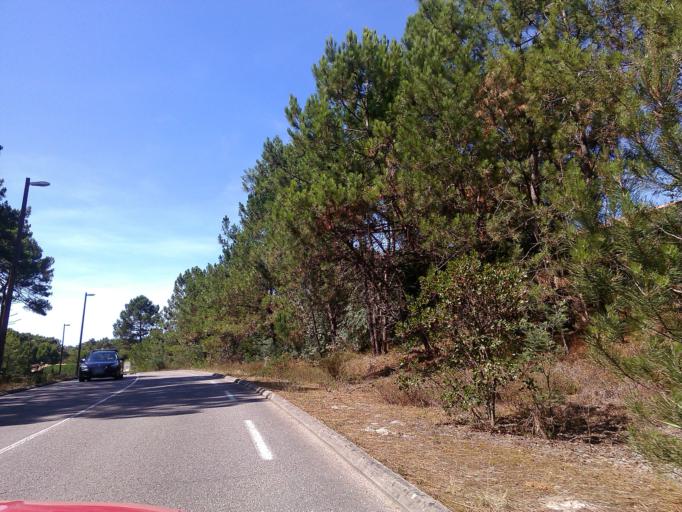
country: FR
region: Aquitaine
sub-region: Departement de la Gironde
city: Lacanau
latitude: 45.0059
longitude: -1.1902
